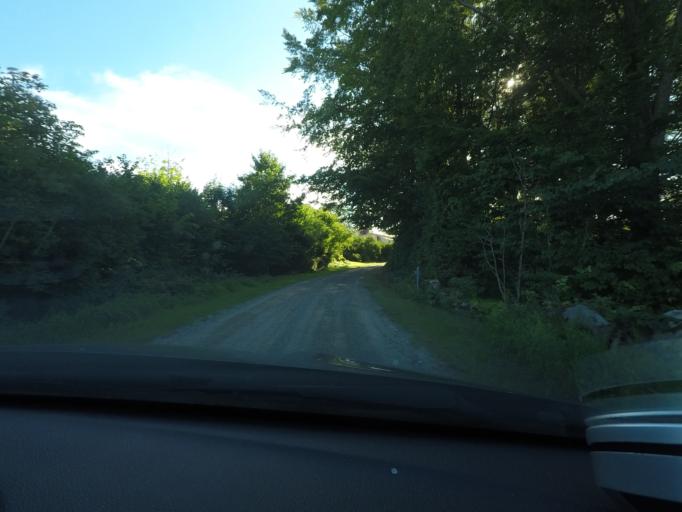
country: SE
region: Skane
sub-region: Hassleholms Kommun
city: Hassleholm
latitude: 56.1179
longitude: 13.8226
